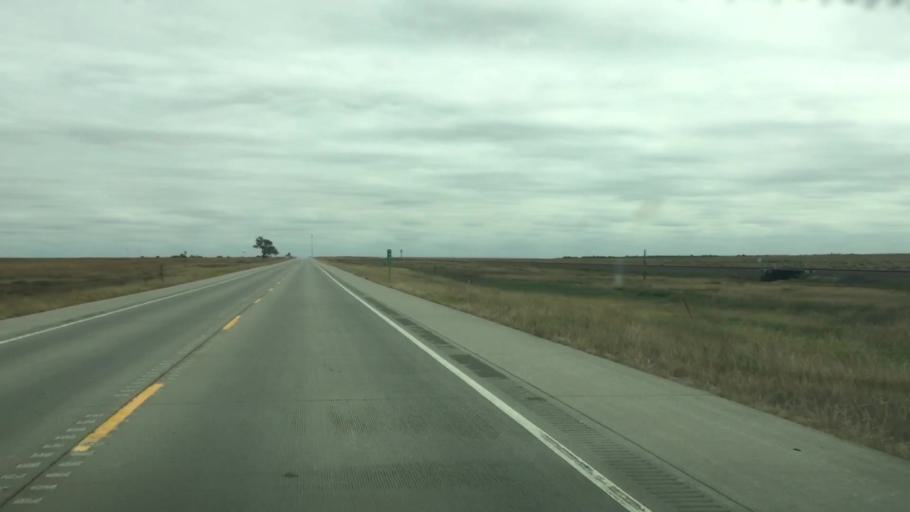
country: US
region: Colorado
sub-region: Kiowa County
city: Eads
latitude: 38.7649
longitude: -102.8359
